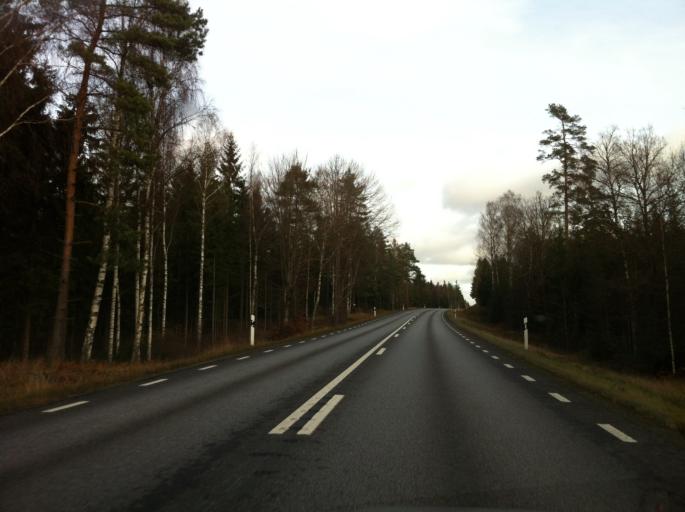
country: SE
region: Kronoberg
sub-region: Alvesta Kommun
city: Vislanda
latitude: 56.7643
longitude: 14.5265
